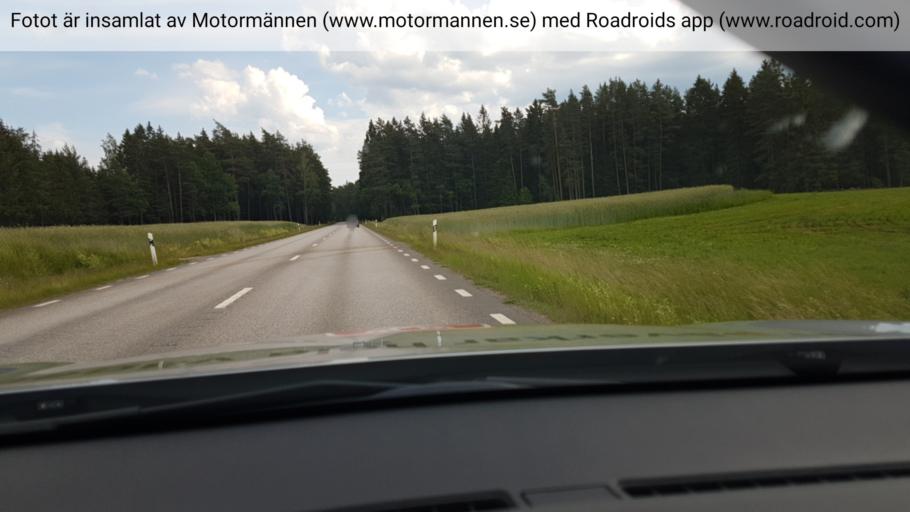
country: SE
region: Vaestra Goetaland
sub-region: Tibro Kommun
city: Tibro
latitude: 58.3457
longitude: 14.1485
